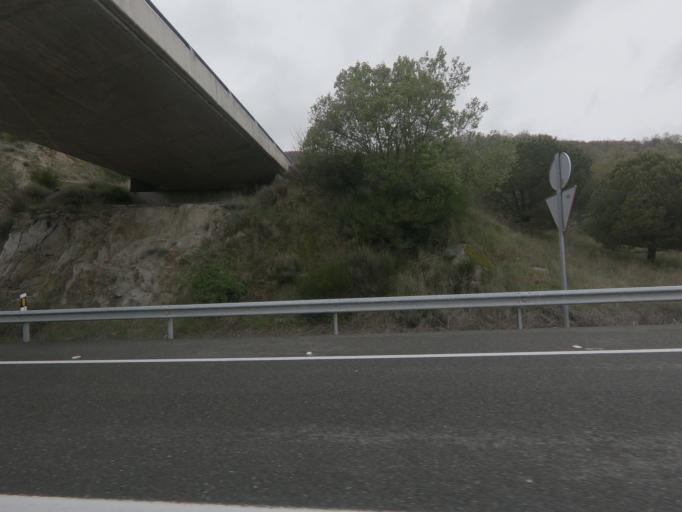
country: ES
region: Extremadura
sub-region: Provincia de Caceres
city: Banos de Montemayor
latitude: 40.3245
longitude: -5.8630
